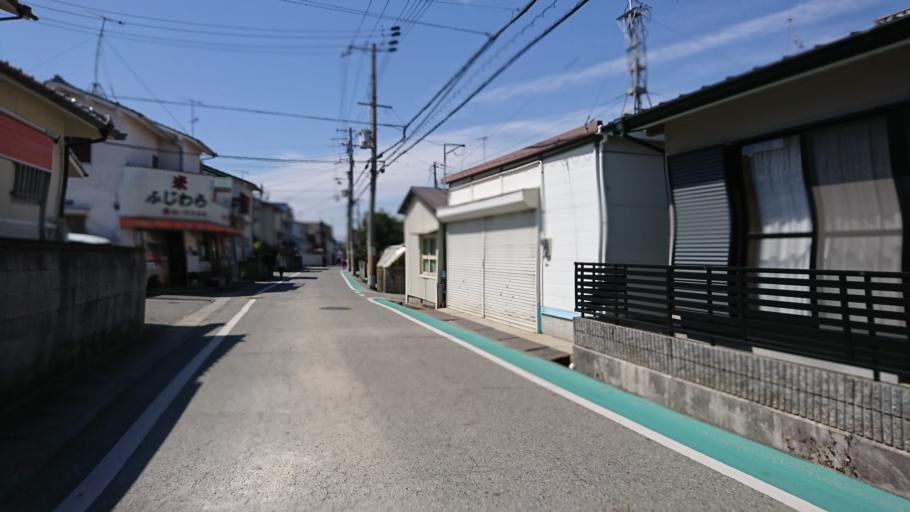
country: JP
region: Hyogo
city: Kakogawacho-honmachi
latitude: 34.7475
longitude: 134.8764
